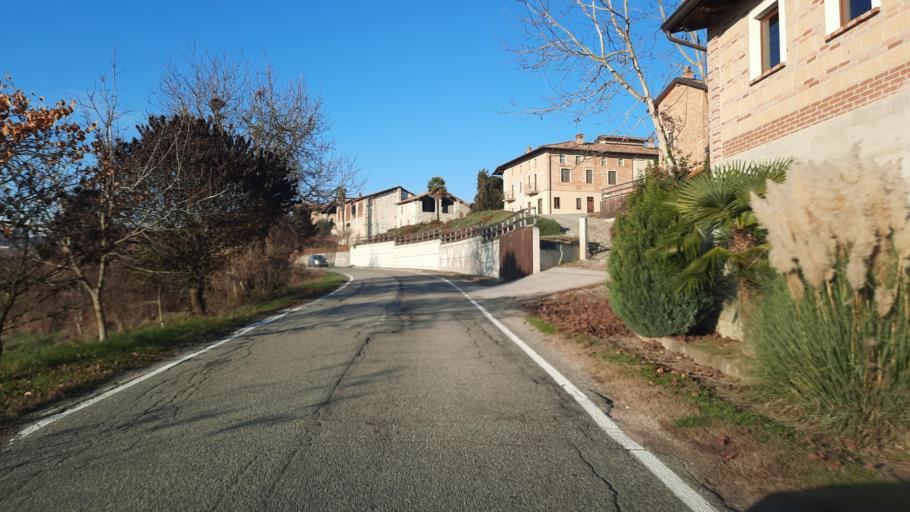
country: IT
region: Piedmont
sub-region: Provincia di Alessandria
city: Camino
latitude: 45.1562
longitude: 8.2931
